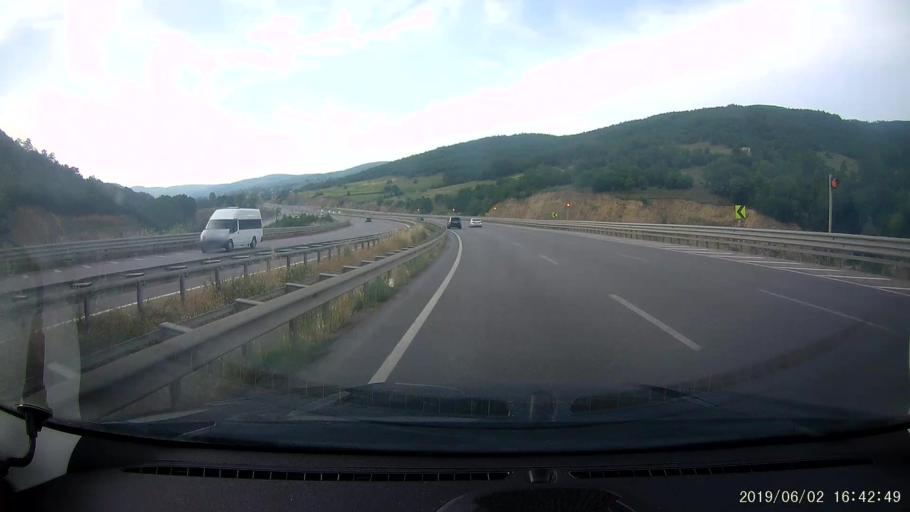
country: TR
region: Samsun
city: Kavak
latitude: 41.1243
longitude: 36.1379
